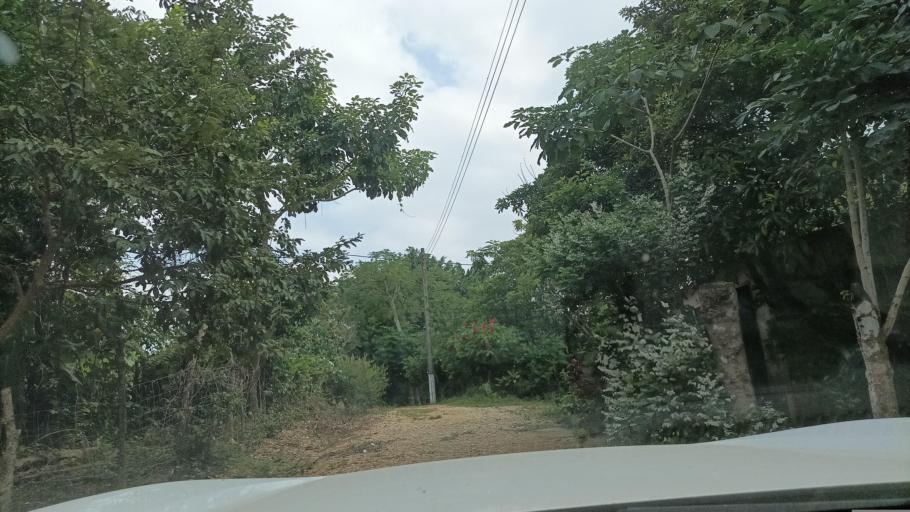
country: MX
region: Veracruz
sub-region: Texistepec
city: Venustiano Carranza (Pena Blanca)
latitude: 17.5400
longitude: -94.6599
